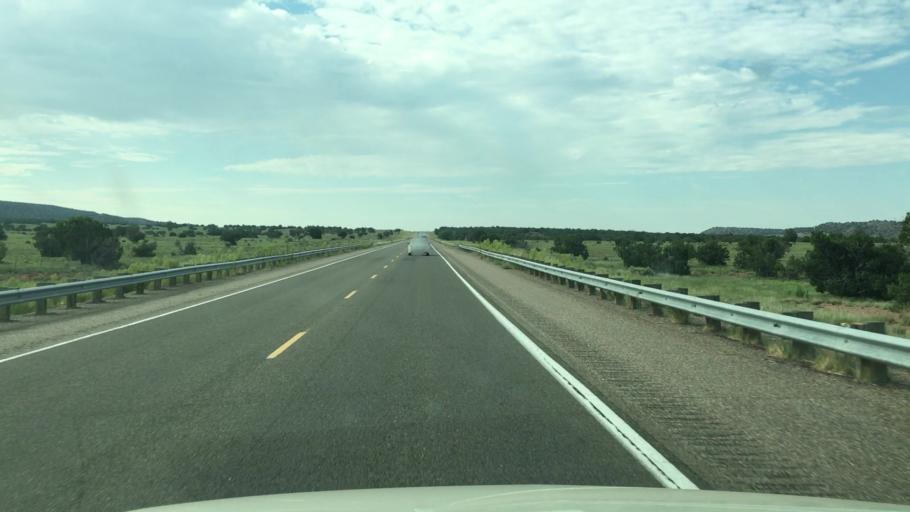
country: US
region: New Mexico
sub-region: Santa Fe County
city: Eldorado at Santa Fe
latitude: 35.3231
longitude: -105.8324
